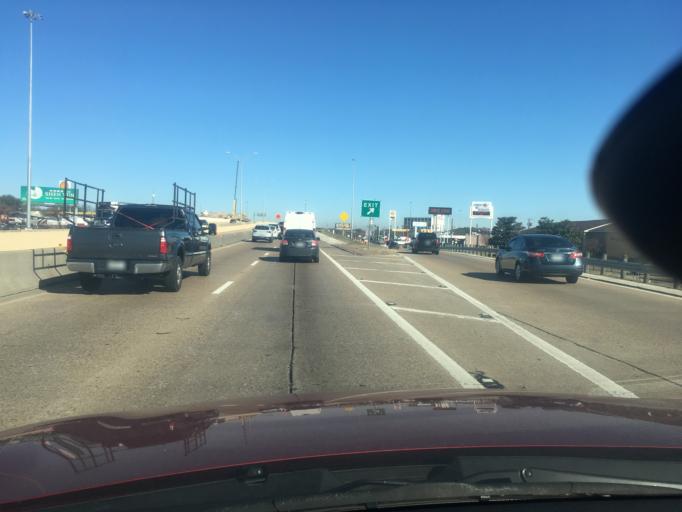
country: US
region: Texas
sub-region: Dallas County
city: Cockrell Hill
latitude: 32.7027
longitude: -96.8340
